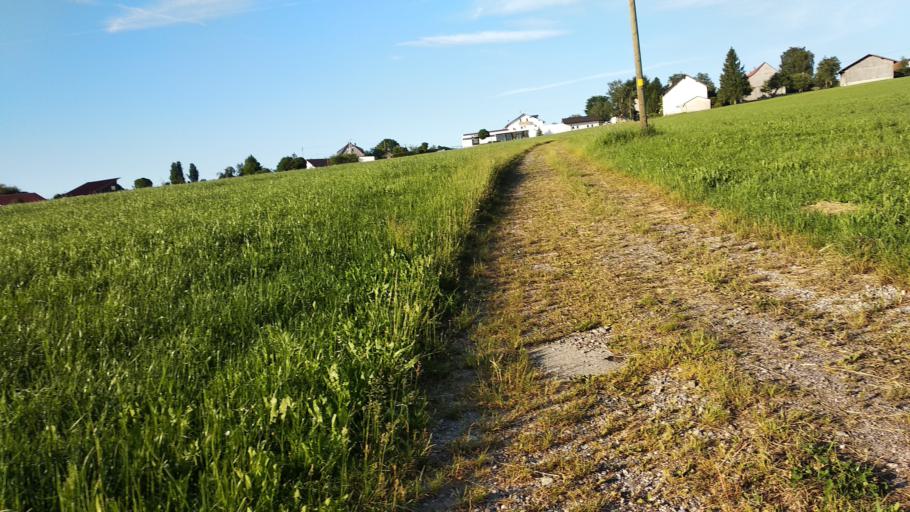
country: DE
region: Bavaria
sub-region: Swabia
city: Kronburg
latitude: 47.9055
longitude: 10.1483
